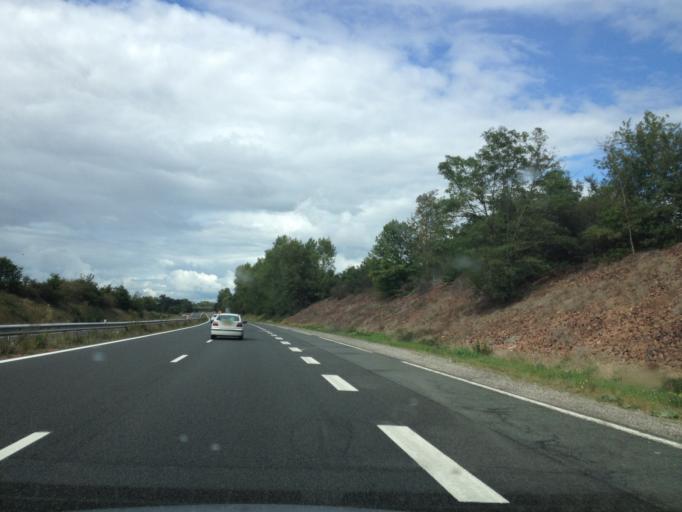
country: FR
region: Rhone-Alpes
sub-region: Departement de la Loire
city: Le Coteau
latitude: 45.9948
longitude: 4.1152
